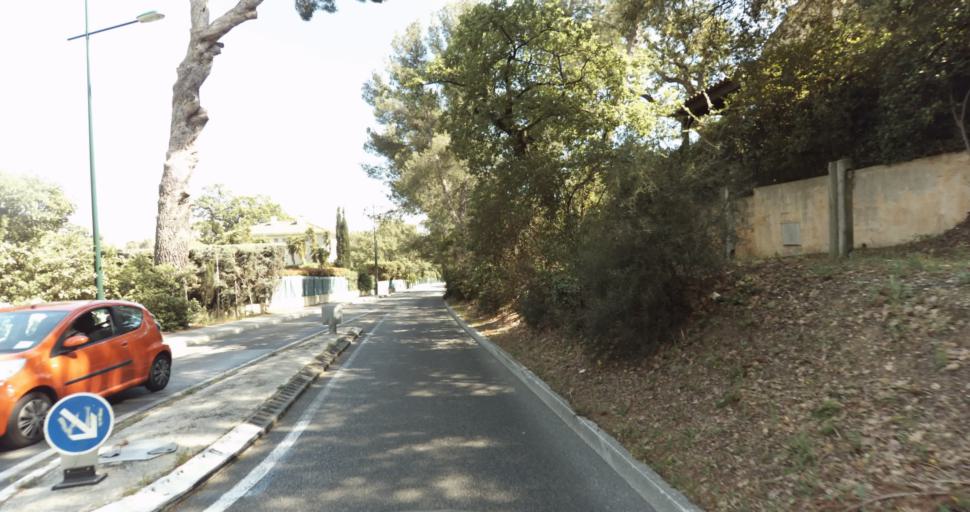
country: FR
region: Provence-Alpes-Cote d'Azur
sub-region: Departement du Var
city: Hyeres
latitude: 43.0958
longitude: 6.1237
